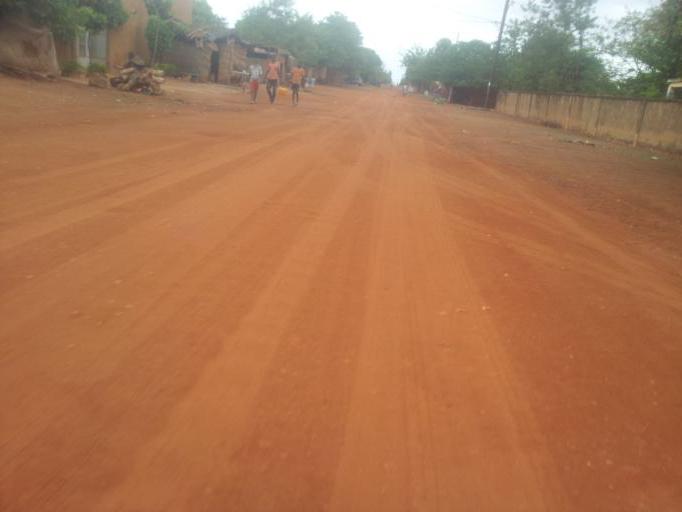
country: BF
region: Centre
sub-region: Kadiogo Province
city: Ouagadougou
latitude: 12.3852
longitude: -1.5459
